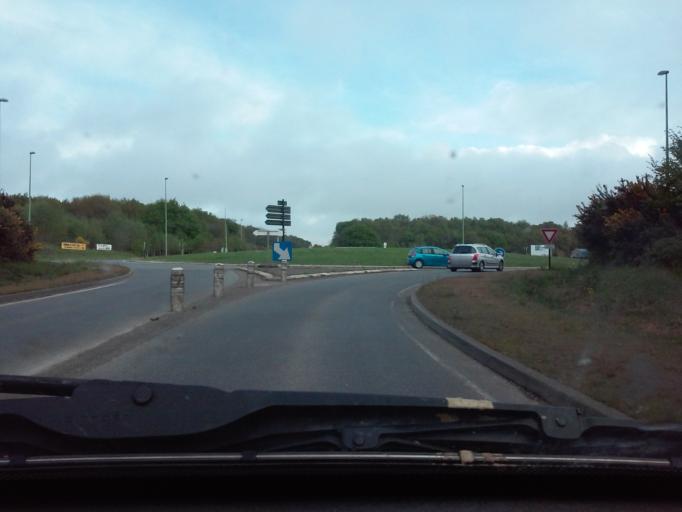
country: FR
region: Brittany
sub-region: Departement d'Ille-et-Vilaine
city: Pleurtuit
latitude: 48.5674
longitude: -2.0609
